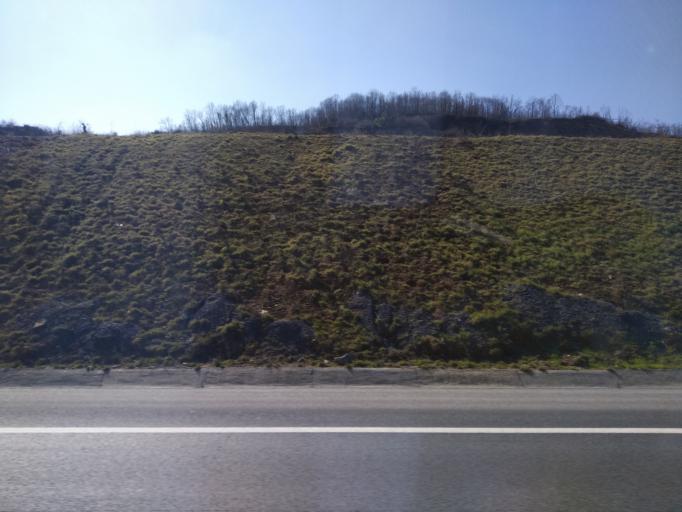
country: TR
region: Istanbul
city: Mahmut Sevket Pasa
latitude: 41.1605
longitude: 29.2599
